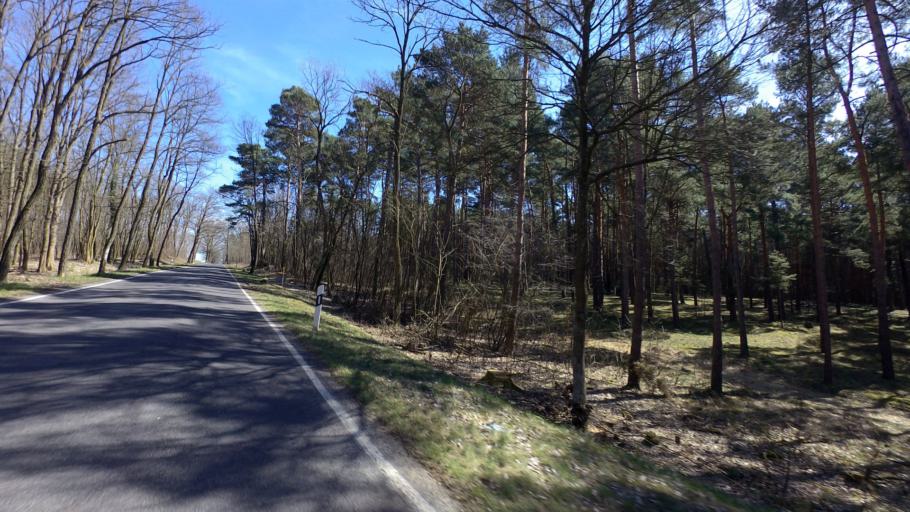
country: DE
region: Brandenburg
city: Munchehofe
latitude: 52.1601
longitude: 13.8842
